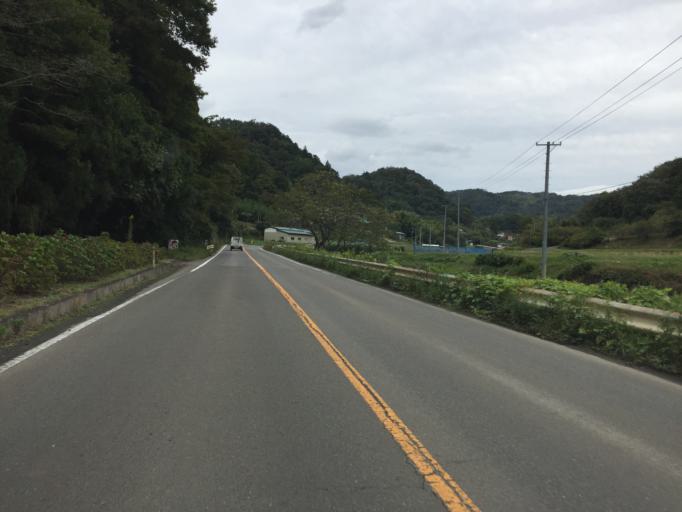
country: JP
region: Fukushima
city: Yanagawamachi-saiwaicho
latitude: 37.8737
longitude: 140.6463
